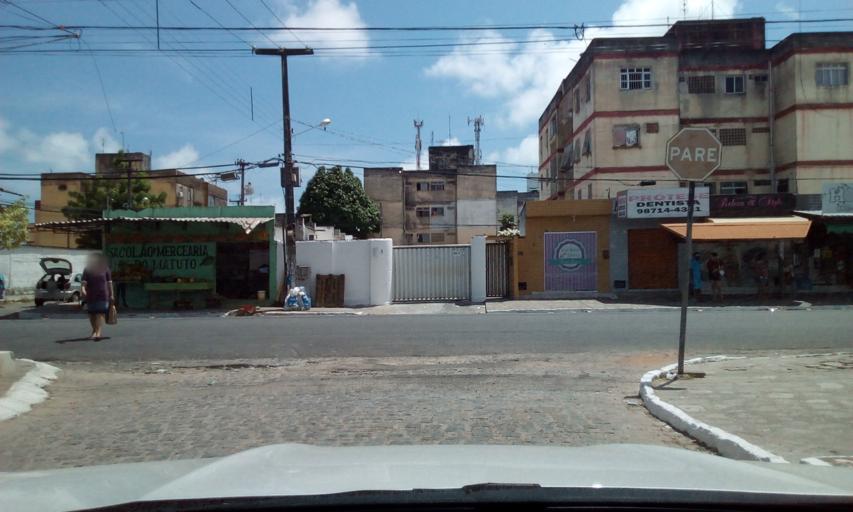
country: BR
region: Paraiba
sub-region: Joao Pessoa
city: Joao Pessoa
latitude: -7.1651
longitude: -34.8344
